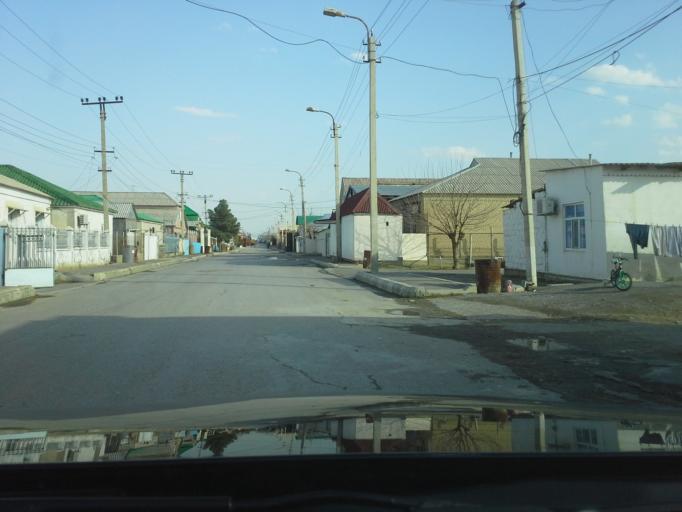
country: TM
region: Ahal
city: Abadan
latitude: 38.0204
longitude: 58.2262
